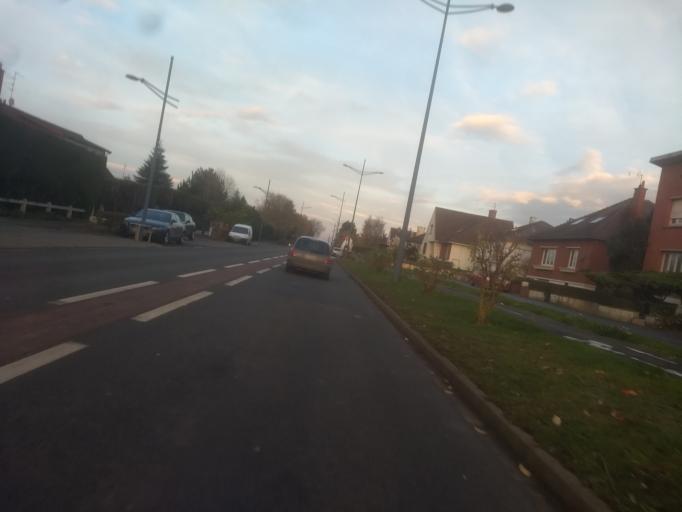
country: FR
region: Nord-Pas-de-Calais
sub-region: Departement du Pas-de-Calais
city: Dainville
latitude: 50.2769
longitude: 2.7256
